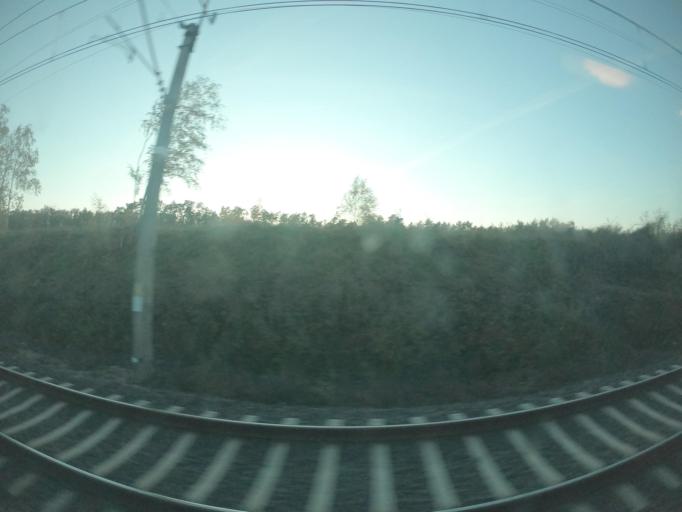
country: PL
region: West Pomeranian Voivodeship
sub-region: Powiat mysliborski
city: Boleszkowice
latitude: 52.7254
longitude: 14.5253
